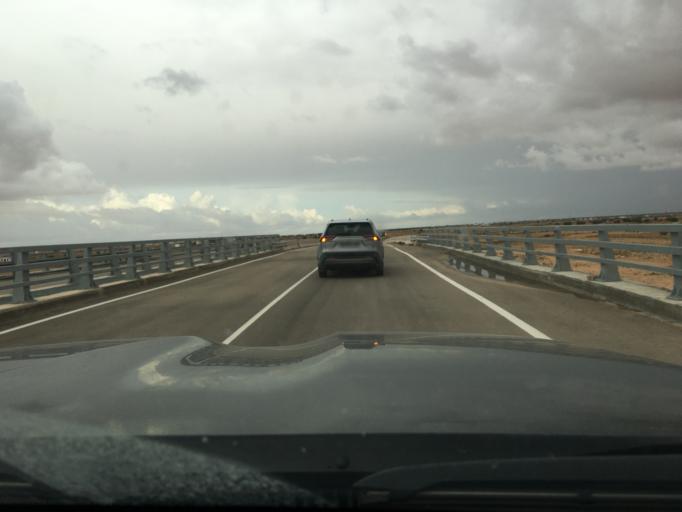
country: TN
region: Madanin
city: Medenine
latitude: 33.2994
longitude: 10.6090
